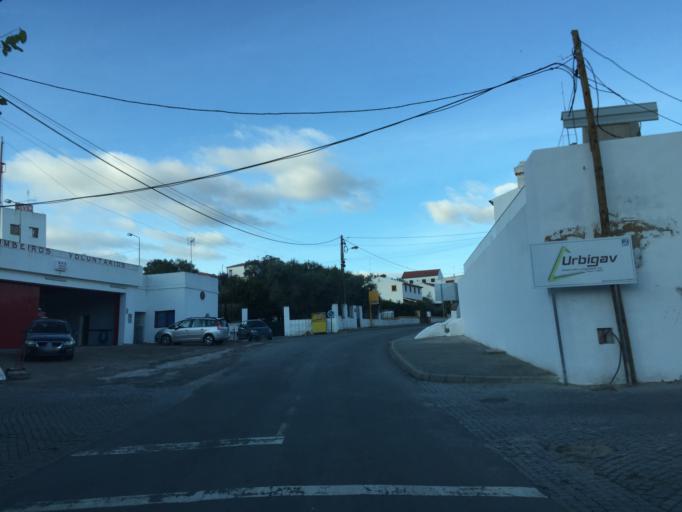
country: PT
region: Portalegre
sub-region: Alter do Chao
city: Alter do Chao
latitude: 39.2865
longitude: -7.6476
